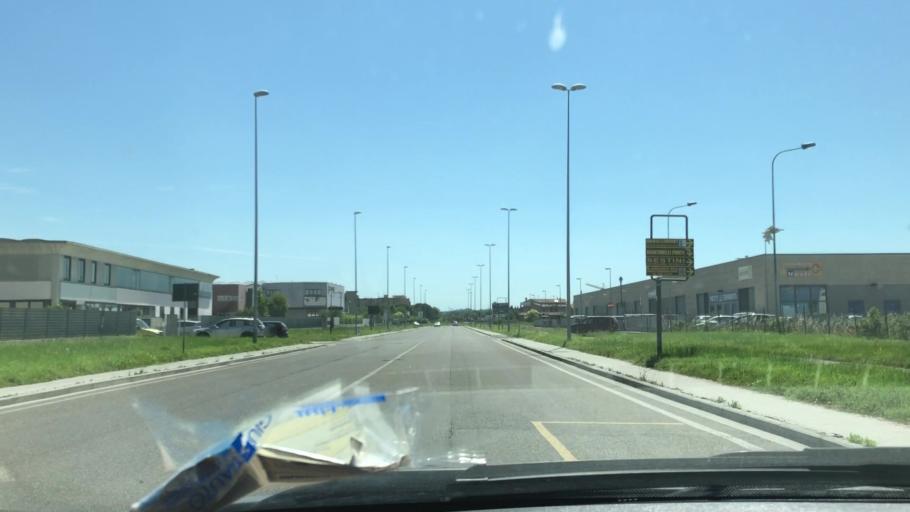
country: IT
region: Tuscany
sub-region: Province of Pisa
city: Pontedera
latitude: 43.6564
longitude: 10.6192
